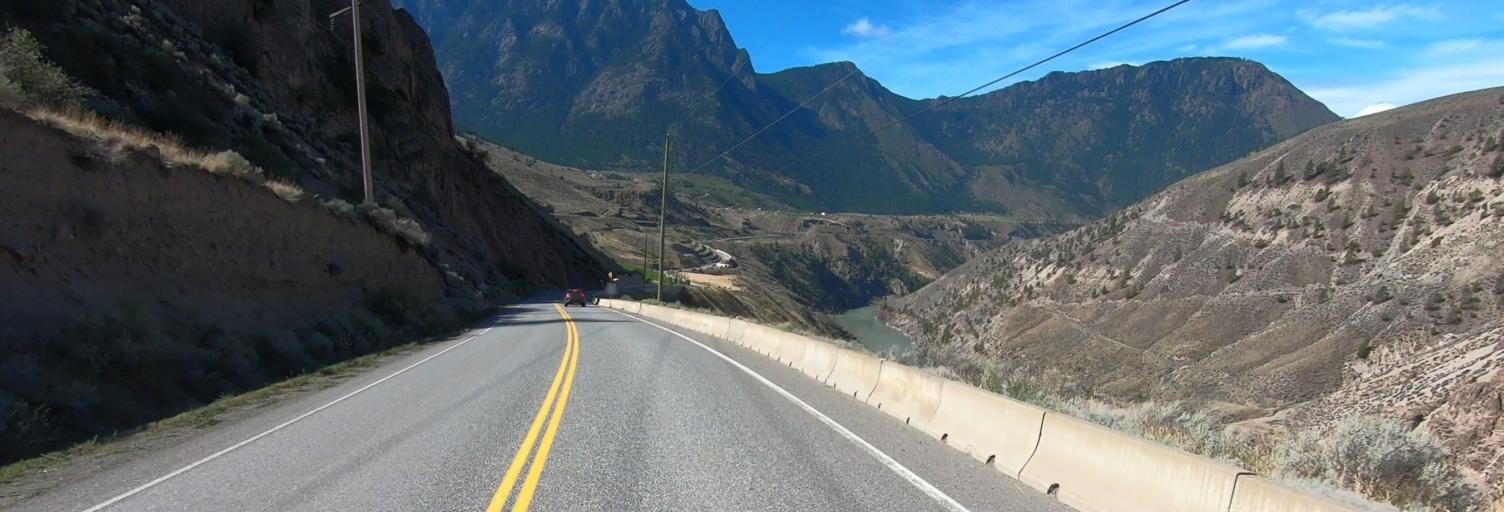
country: CA
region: British Columbia
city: Lillooet
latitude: 50.7538
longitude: -121.8390
